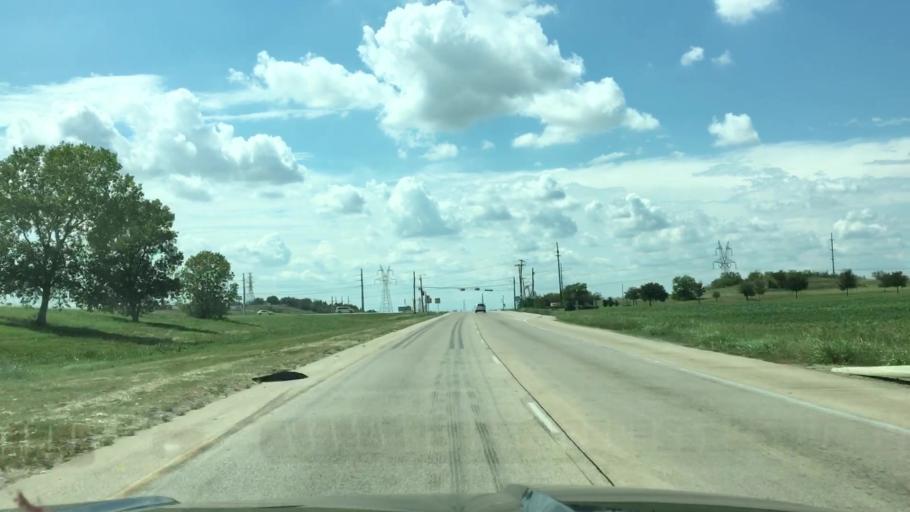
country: US
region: Texas
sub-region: Denton County
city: Roanoke
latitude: 33.0157
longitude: -97.2324
